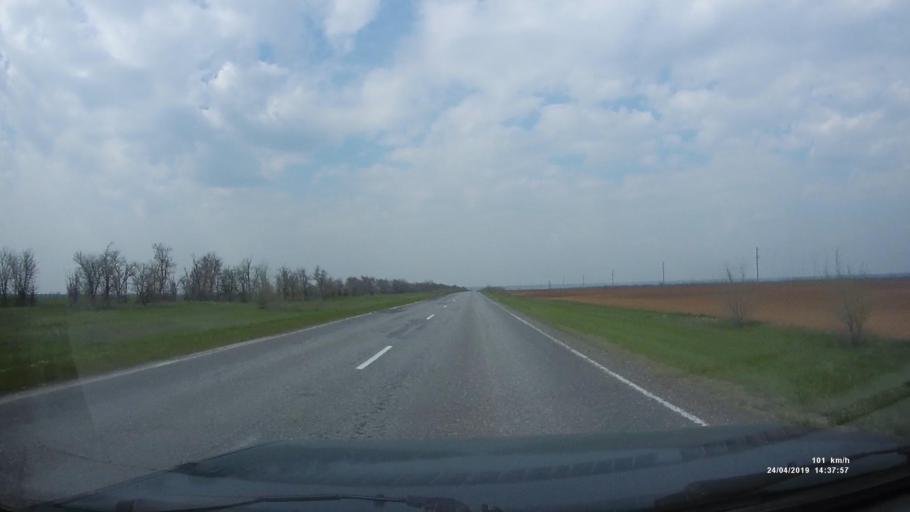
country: RU
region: Rostov
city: Remontnoye
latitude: 46.3938
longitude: 43.8863
